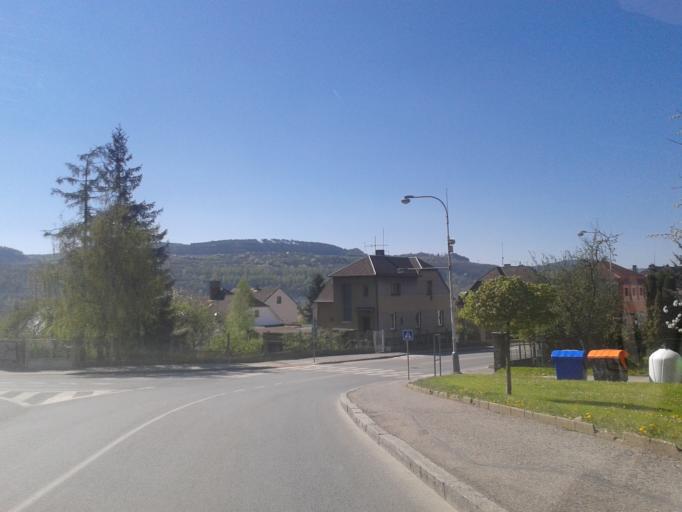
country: CZ
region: Central Bohemia
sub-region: Okres Beroun
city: Beroun
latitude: 49.9617
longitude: 14.0610
